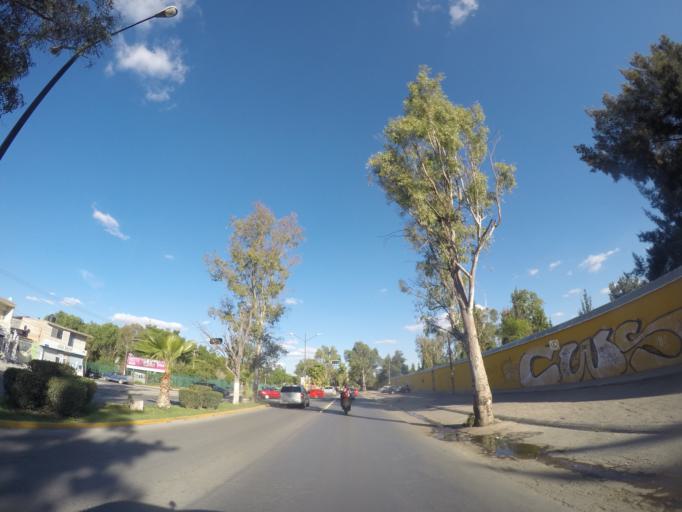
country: MX
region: San Luis Potosi
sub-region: San Luis Potosi
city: San Luis Potosi
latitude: 22.1816
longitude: -100.9985
